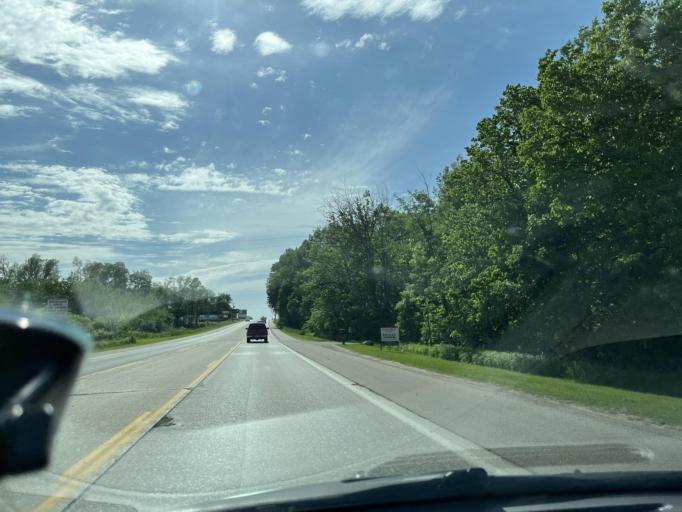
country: US
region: Michigan
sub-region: Barry County
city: Hastings
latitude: 42.6458
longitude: -85.3262
